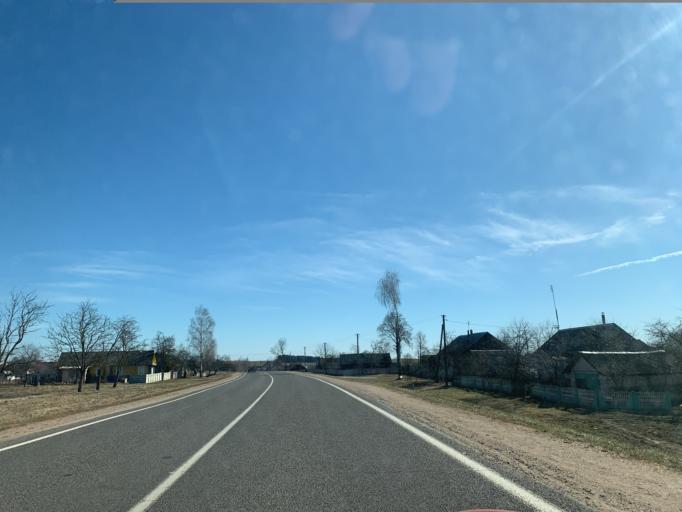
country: BY
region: Minsk
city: Nyasvizh
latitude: 53.2267
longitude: 26.7573
